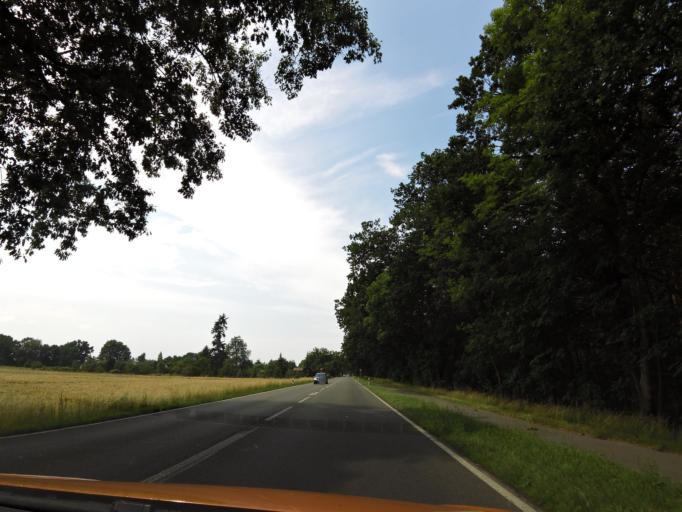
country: DE
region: Brandenburg
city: Wusterhausen
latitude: 52.9126
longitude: 12.4394
